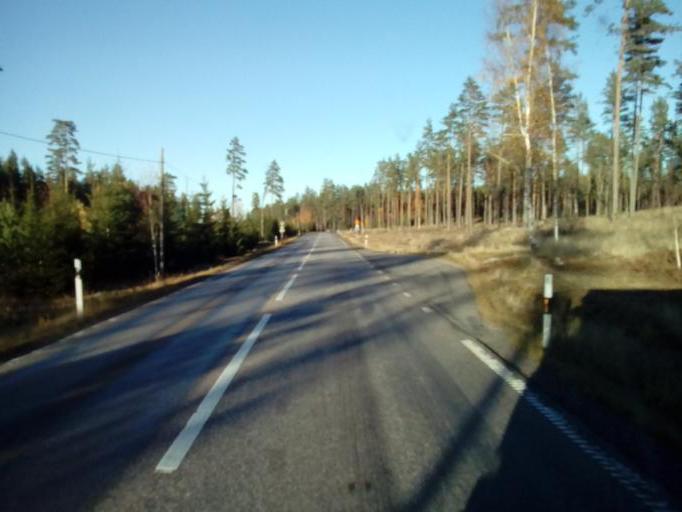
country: SE
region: OErebro
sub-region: Hallsbergs Kommun
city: Palsboda
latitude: 58.8542
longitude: 15.4048
